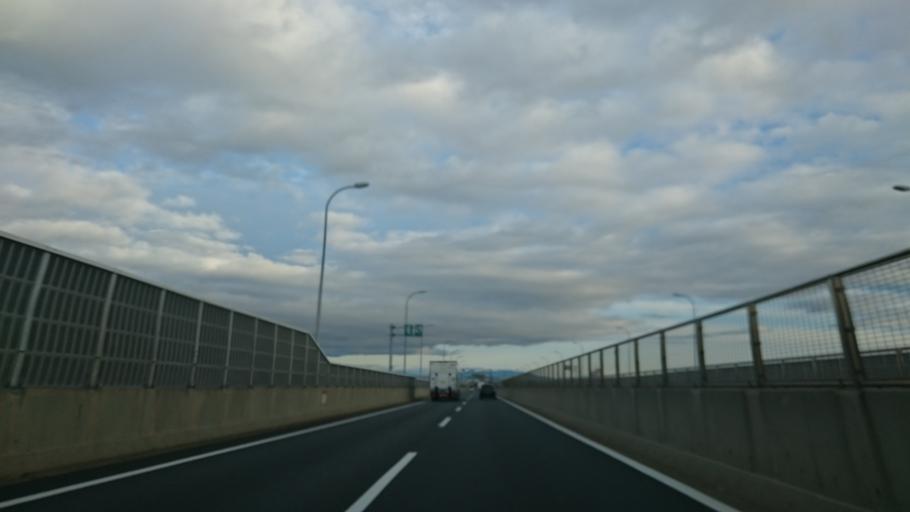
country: JP
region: Aichi
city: Komaki
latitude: 35.2452
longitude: 136.9085
